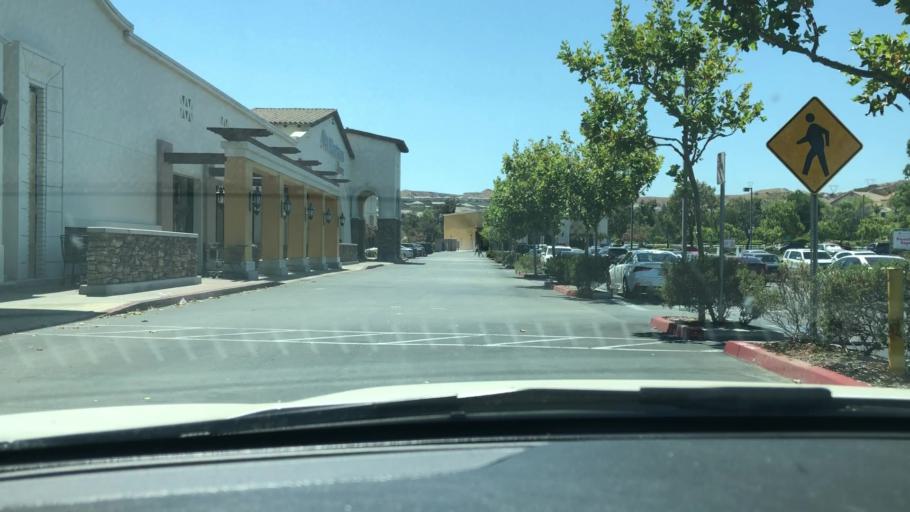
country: US
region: California
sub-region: Los Angeles County
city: Valencia
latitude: 34.4625
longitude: -118.5563
